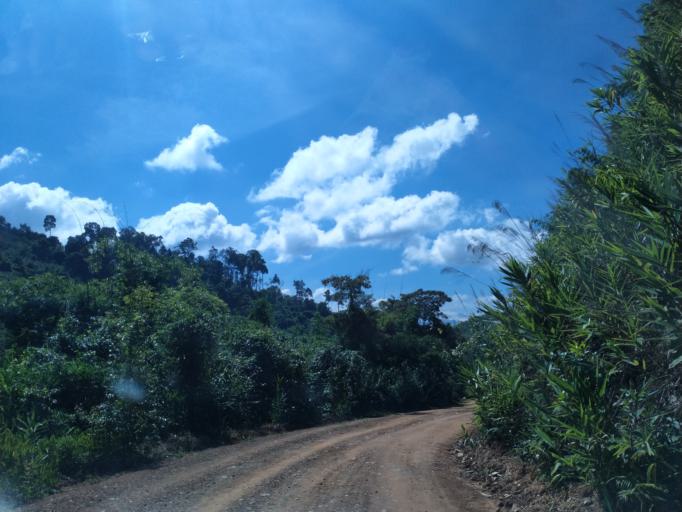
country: LA
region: Vientiane
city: Muang Phon-Hong
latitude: 18.6303
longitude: 102.8798
